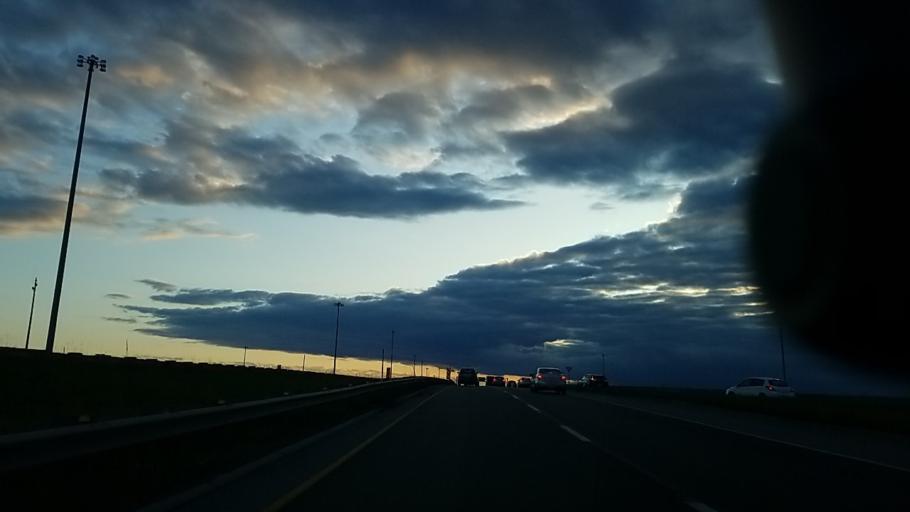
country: CA
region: Quebec
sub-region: Laval
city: Laval
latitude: 45.5773
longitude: -73.7495
